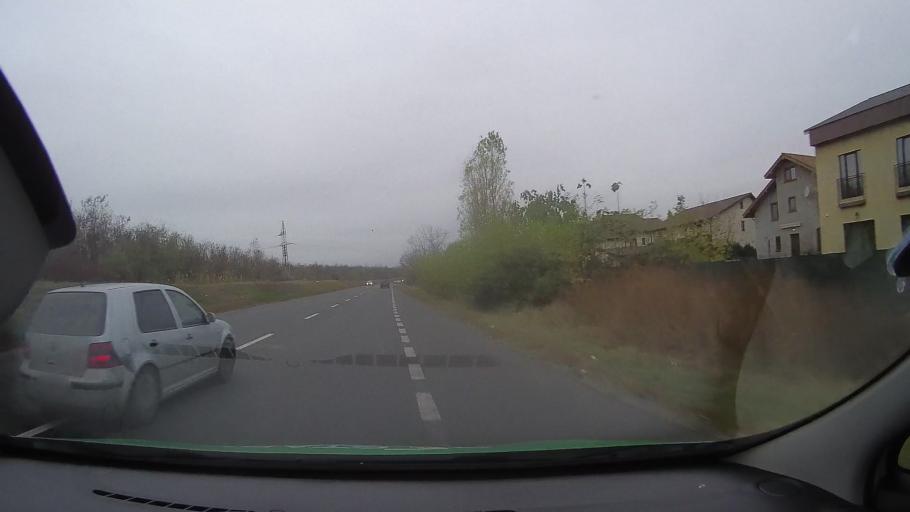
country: RO
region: Ialomita
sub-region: Comuna Slobozia
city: Slobozia
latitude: 44.5568
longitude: 27.3669
